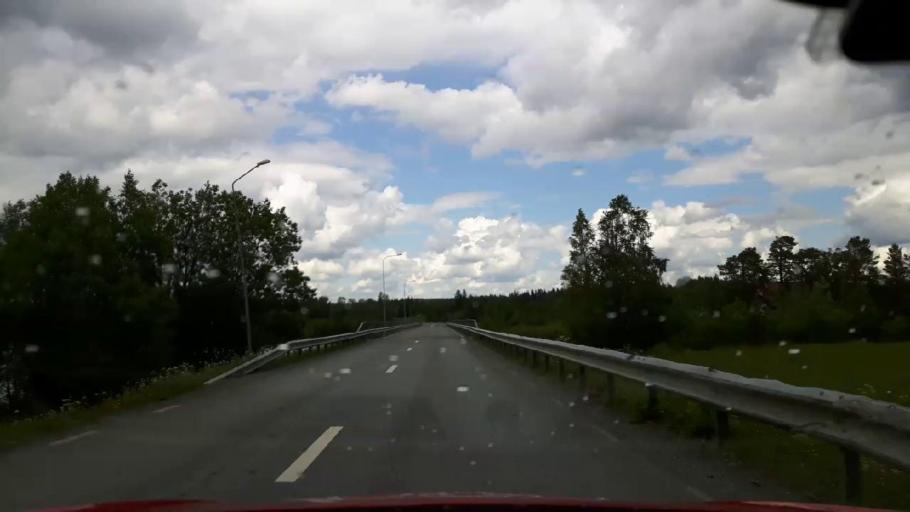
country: SE
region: Jaemtland
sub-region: Krokoms Kommun
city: Krokom
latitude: 63.5490
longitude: 14.2793
